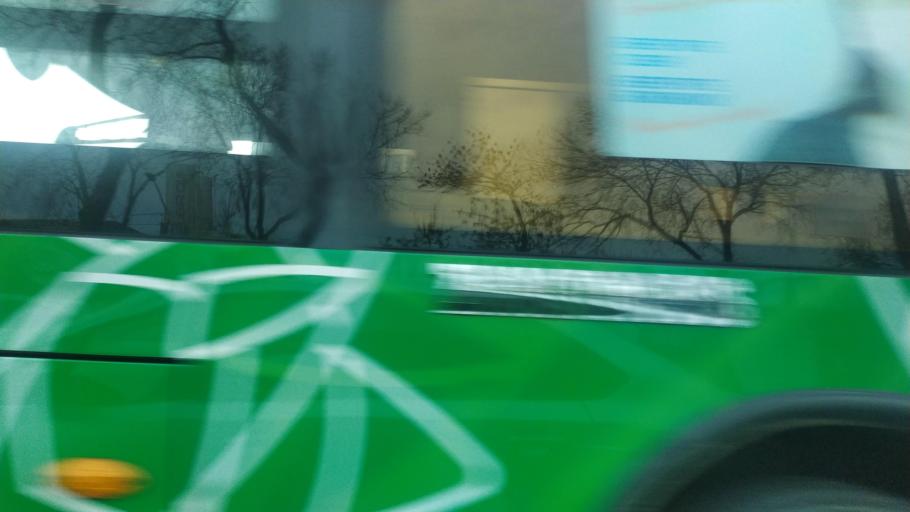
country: KZ
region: Almaty Qalasy
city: Almaty
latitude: 43.2377
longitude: 76.8848
